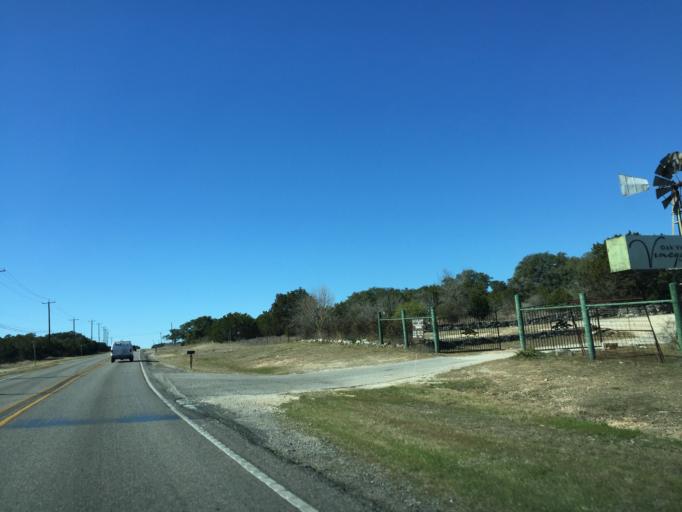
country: US
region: Texas
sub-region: Comal County
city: Garden Ridge
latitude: 29.7036
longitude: -98.3140
